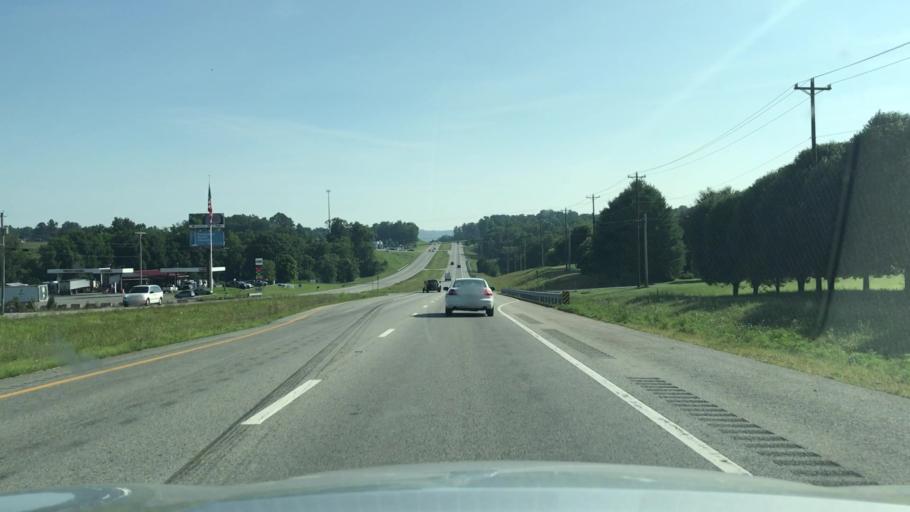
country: US
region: Tennessee
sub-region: Overton County
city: Livingston
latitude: 36.3301
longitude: -85.3560
